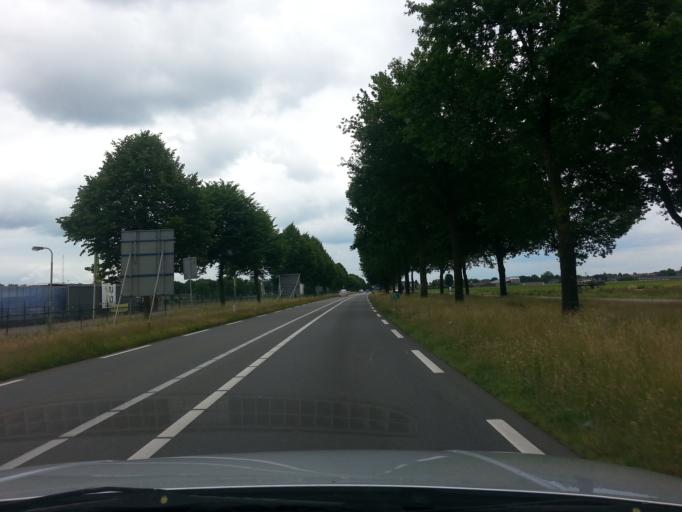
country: NL
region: Limburg
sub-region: Gemeente Venray
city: Venray
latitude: 51.5140
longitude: 5.9666
